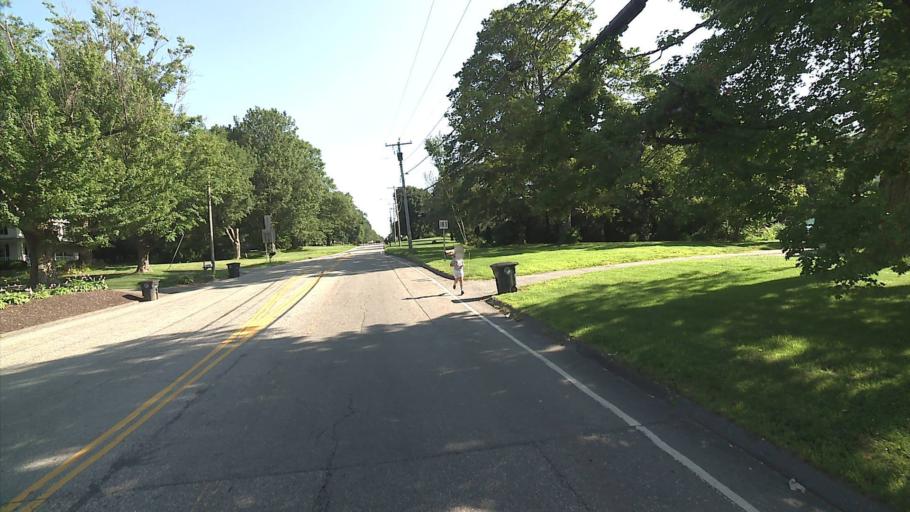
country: US
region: Connecticut
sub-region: Litchfield County
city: Northwest Harwinton
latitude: 41.8216
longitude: -73.0807
